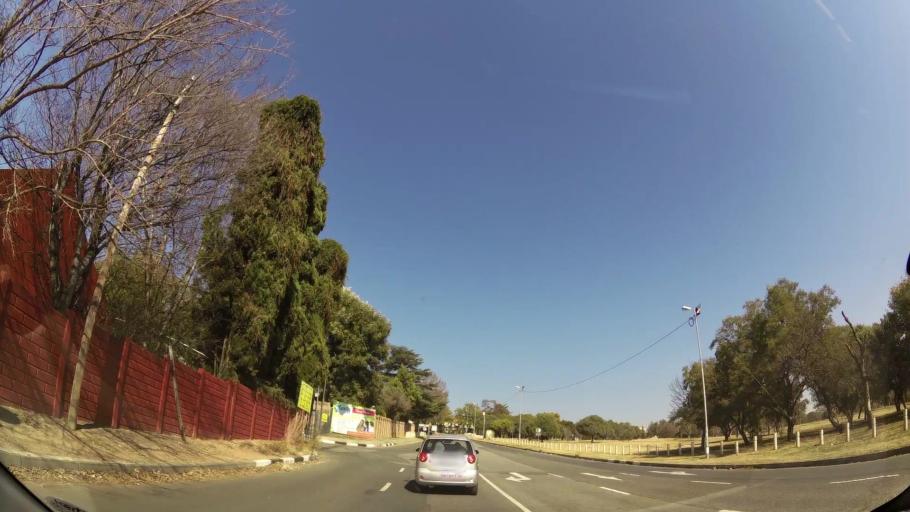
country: ZA
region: Gauteng
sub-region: City of Johannesburg Metropolitan Municipality
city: Johannesburg
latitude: -26.1010
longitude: 28.0367
